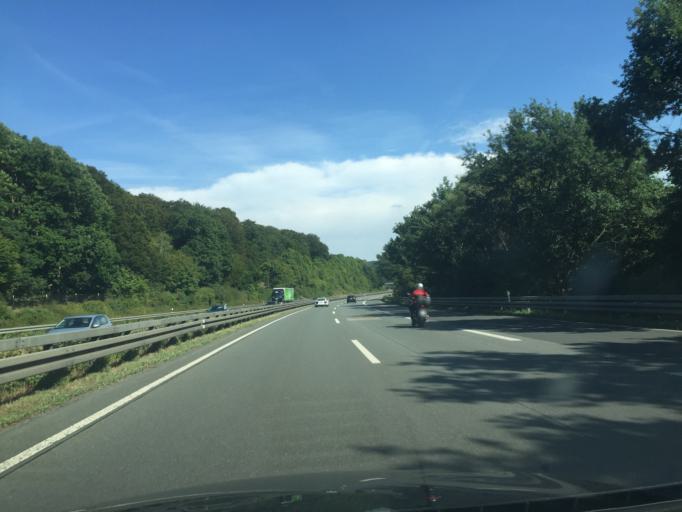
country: DE
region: Hesse
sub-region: Regierungsbezirk Giessen
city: Ehringshausen
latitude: 50.6209
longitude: 8.3693
